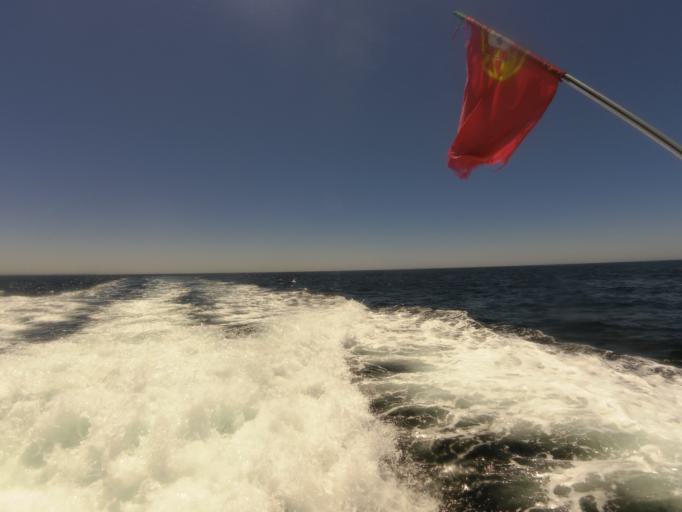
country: PT
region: Leiria
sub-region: Peniche
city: Peniche
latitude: 39.4102
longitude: -9.5017
